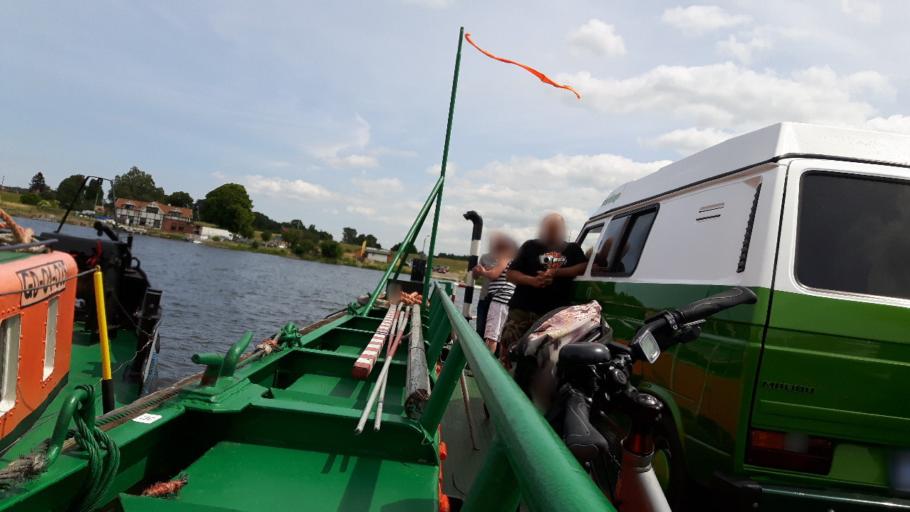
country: PL
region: Pomeranian Voivodeship
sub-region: Powiat nowodworski
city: Ostaszewo
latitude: 54.3330
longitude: 18.9403
